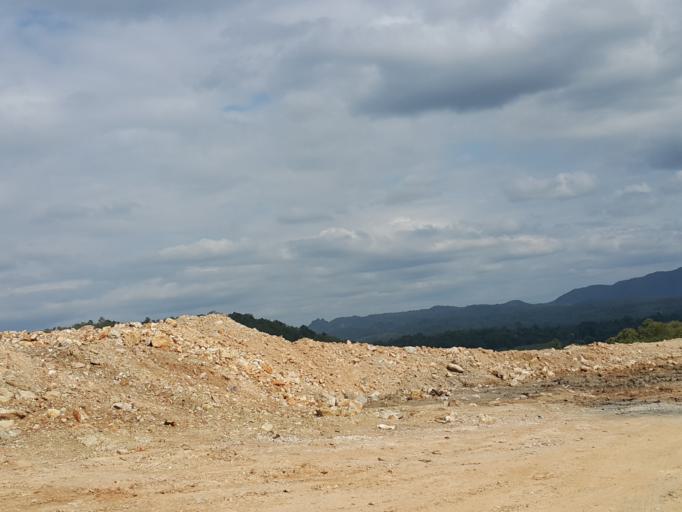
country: TH
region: Lampang
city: Chae Hom
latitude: 18.5713
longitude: 99.4373
